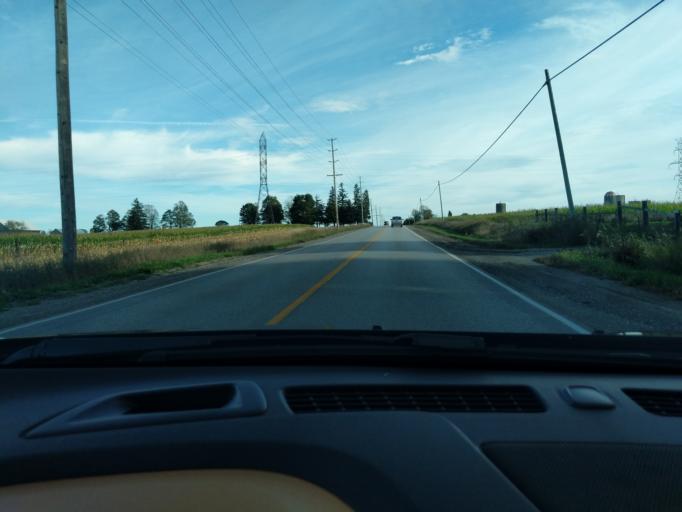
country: CA
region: Ontario
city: Barrie
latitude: 44.4103
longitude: -79.7499
